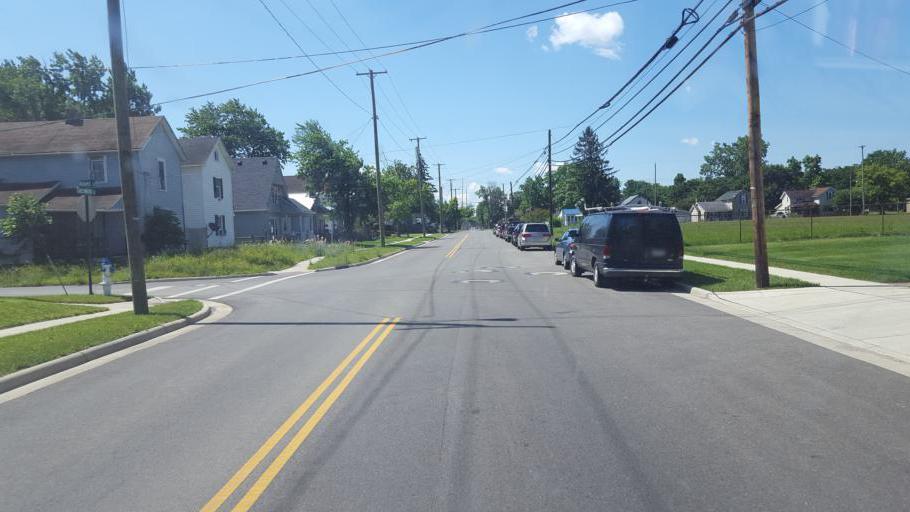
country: US
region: Ohio
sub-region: Marion County
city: Marion
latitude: 40.5963
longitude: -83.1208
